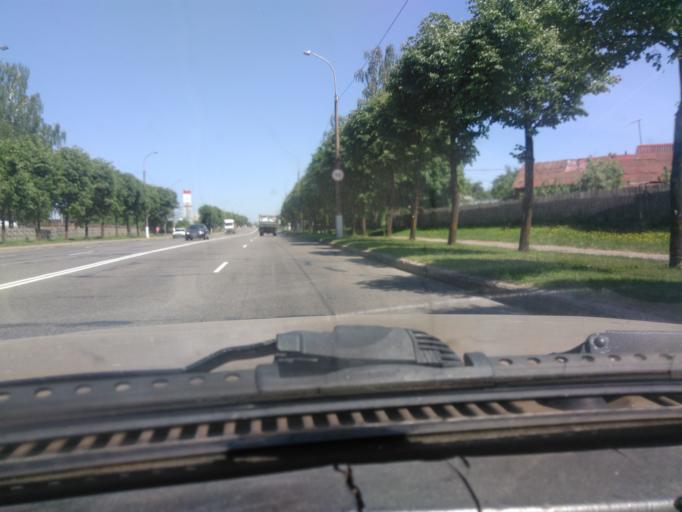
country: BY
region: Mogilev
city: Mahilyow
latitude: 53.9114
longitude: 30.3630
